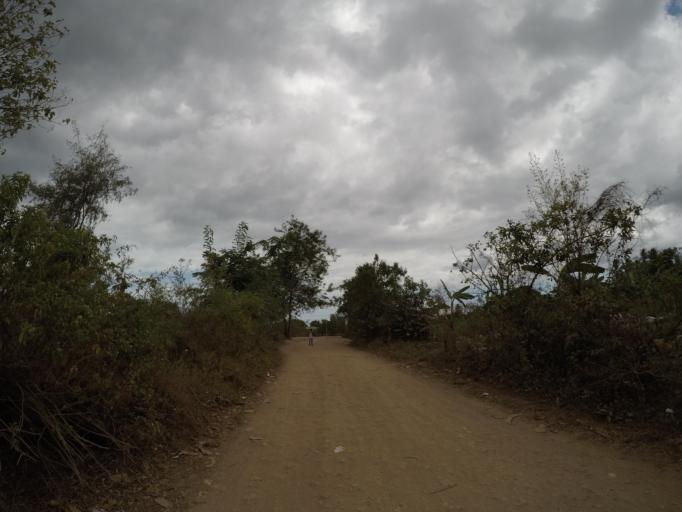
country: TZ
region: Zanzibar Central/South
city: Koani
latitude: -6.1941
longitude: 39.3043
